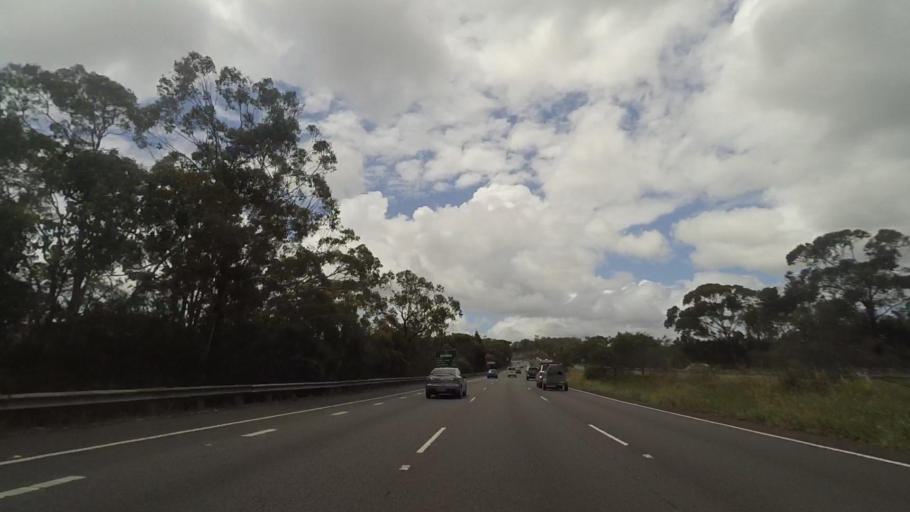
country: AU
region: New South Wales
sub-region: Gosford Shire
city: Point Clare
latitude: -33.4603
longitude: 151.1986
